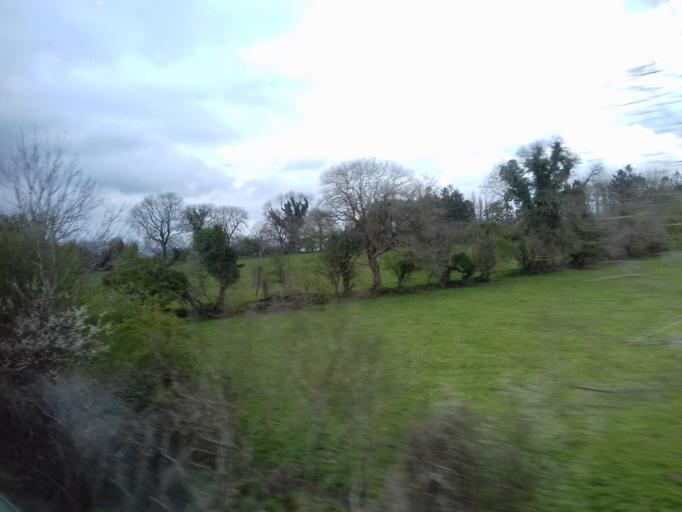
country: IE
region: Leinster
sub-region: An Longfort
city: Longford
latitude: 53.7539
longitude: -7.8263
